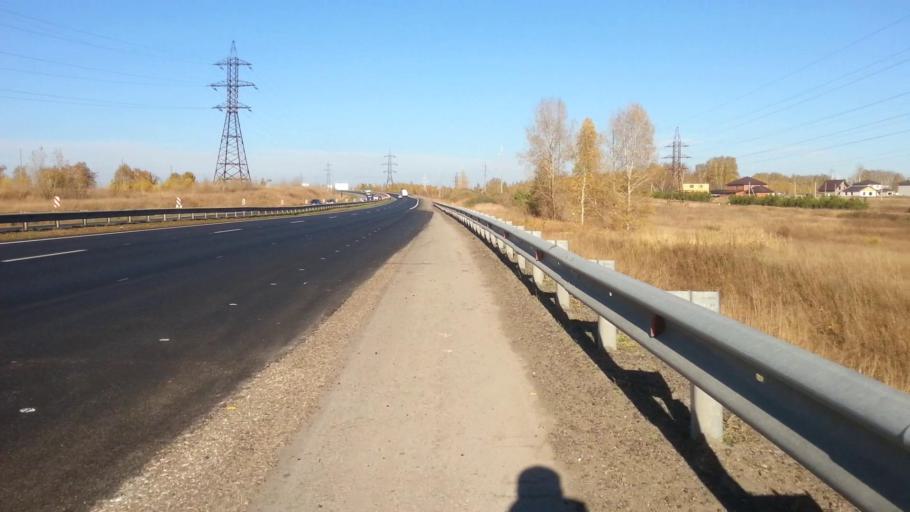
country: RU
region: Altai Krai
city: Sannikovo
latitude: 53.3448
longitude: 83.9425
